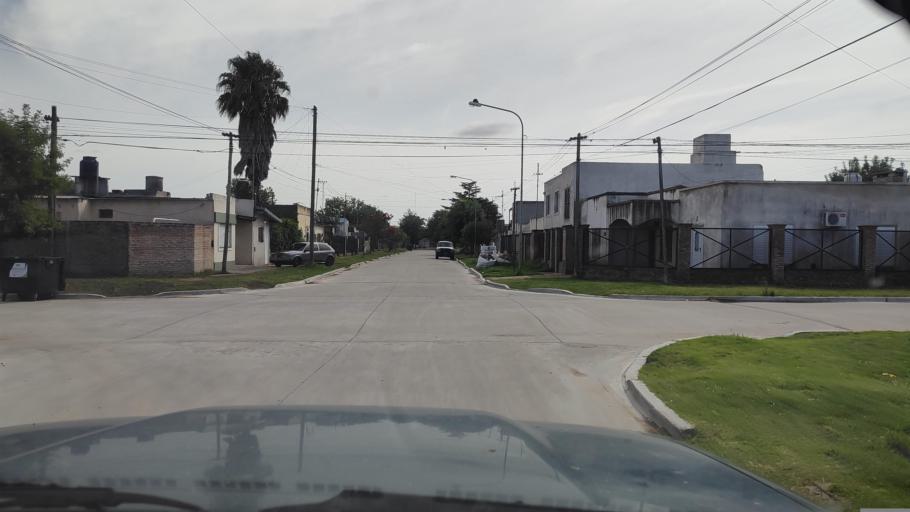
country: AR
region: Buenos Aires
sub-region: Partido de Lujan
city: Lujan
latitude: -34.5790
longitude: -59.1233
